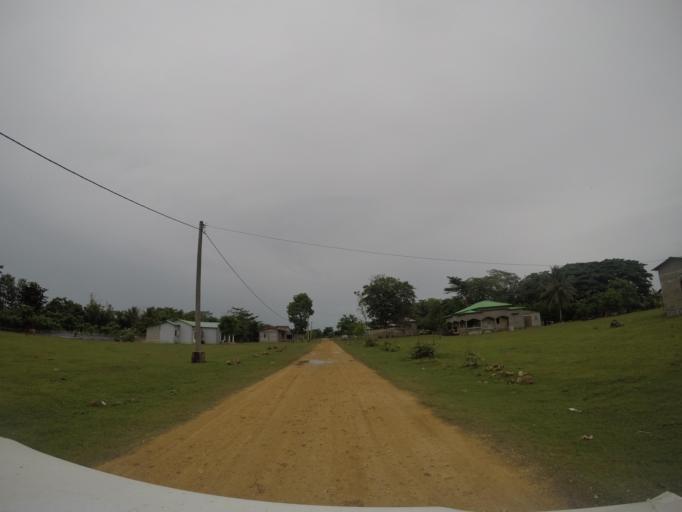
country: TL
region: Lautem
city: Lospalos
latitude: -8.5271
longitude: 127.0103
